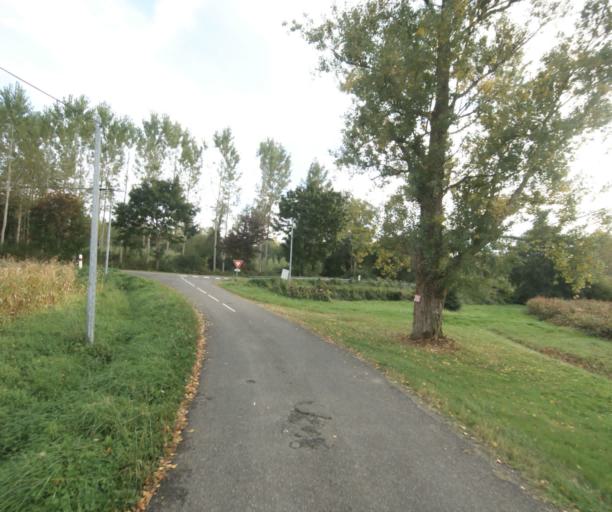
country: FR
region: Midi-Pyrenees
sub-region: Departement du Gers
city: Cazaubon
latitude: 43.8641
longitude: -0.1205
